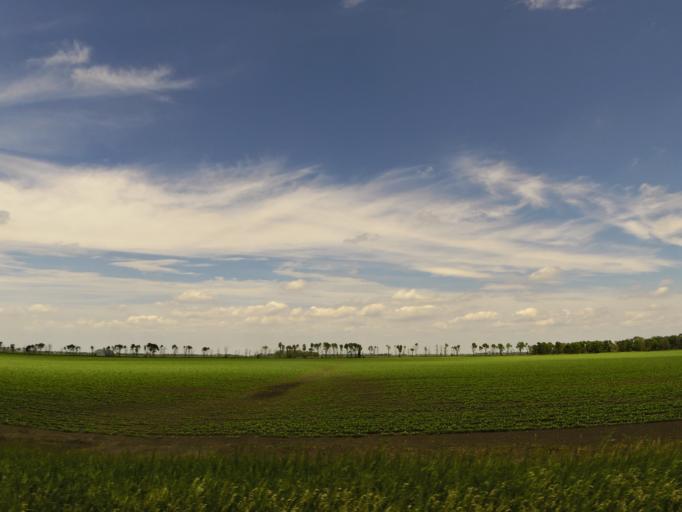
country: US
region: North Dakota
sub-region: Walsh County
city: Grafton
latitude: 48.2954
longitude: -97.2254
